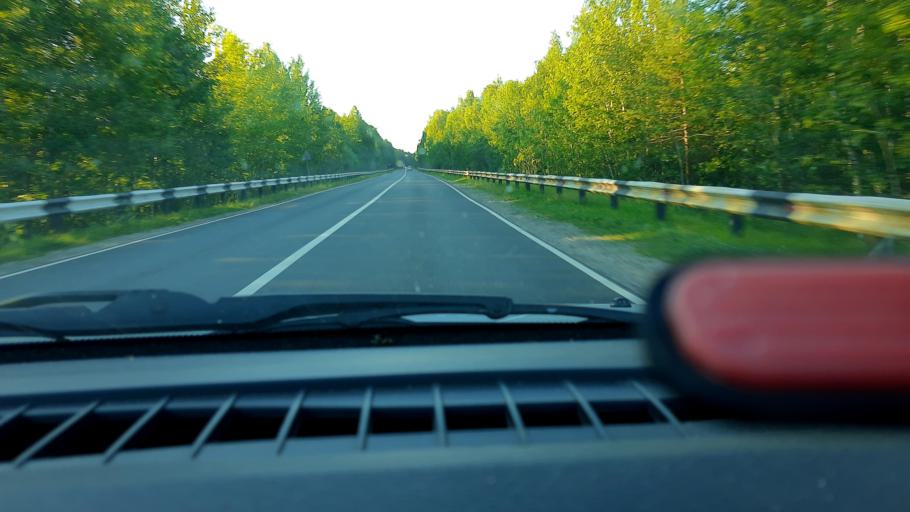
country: RU
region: Nizjnij Novgorod
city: Krasnyye Baki
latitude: 57.1207
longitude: 45.2102
